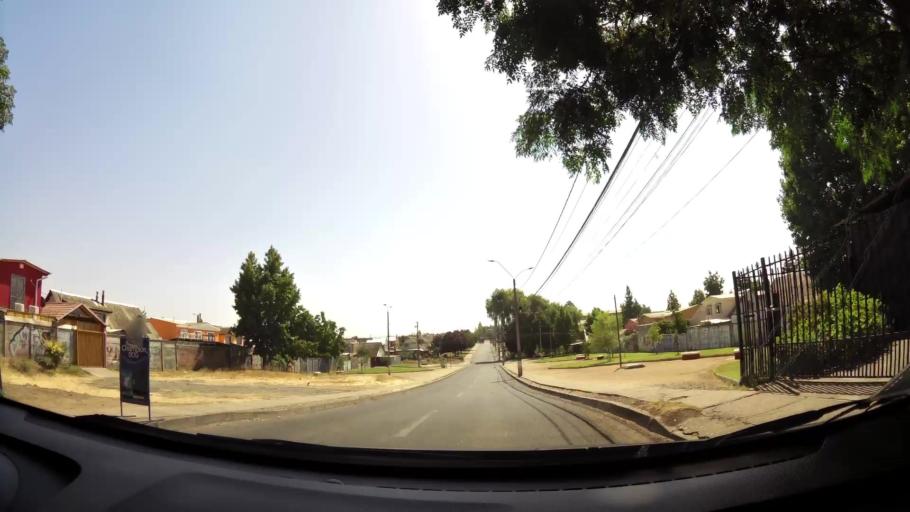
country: CL
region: Maule
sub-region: Provincia de Talca
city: Talca
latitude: -35.4101
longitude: -71.6453
